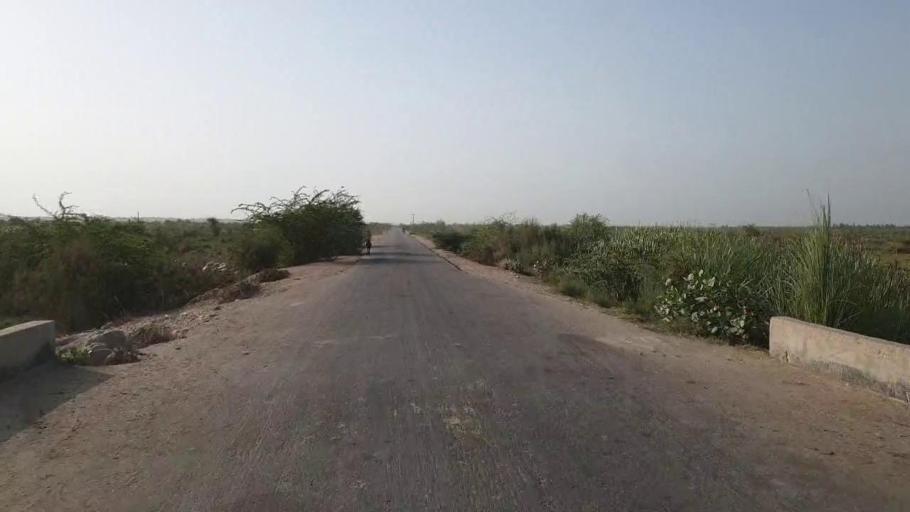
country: PK
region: Sindh
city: Jam Sahib
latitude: 26.4490
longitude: 68.8633
